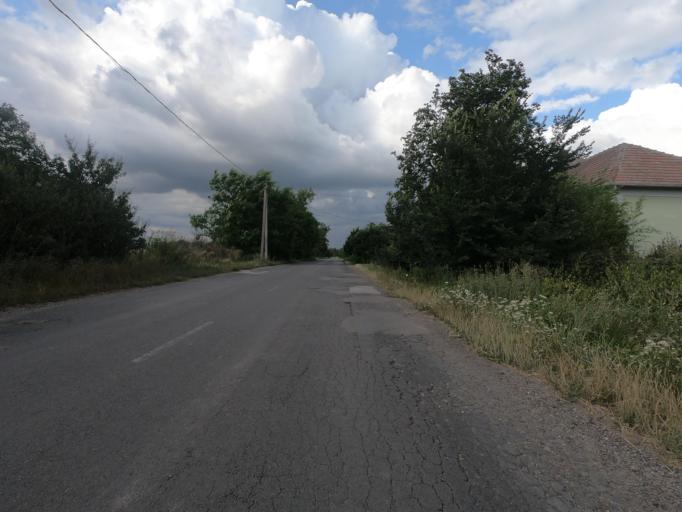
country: HU
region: Heves
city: Poroszlo
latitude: 47.6612
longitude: 20.6592
